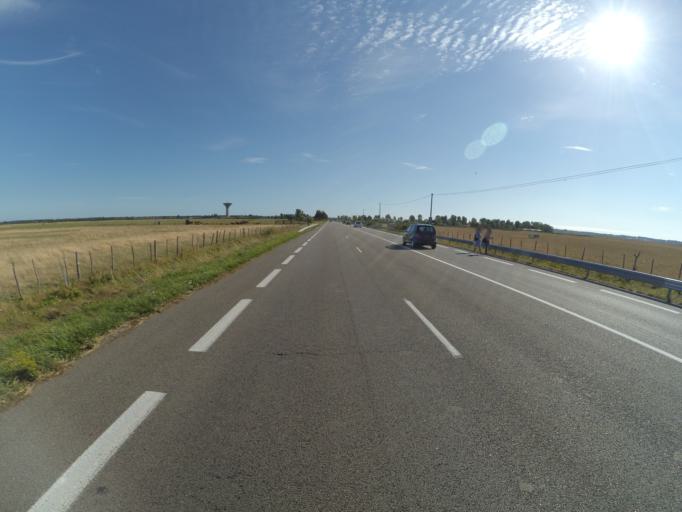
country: FR
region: Pays de la Loire
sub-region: Departement de la Vendee
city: La Tranche-sur-Mer
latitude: 46.3671
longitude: -1.4169
